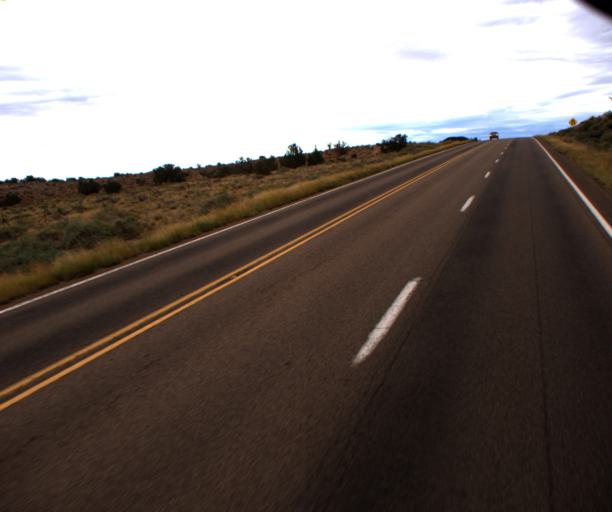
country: US
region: Arizona
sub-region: Navajo County
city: Snowflake
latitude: 34.6919
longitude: -110.1065
